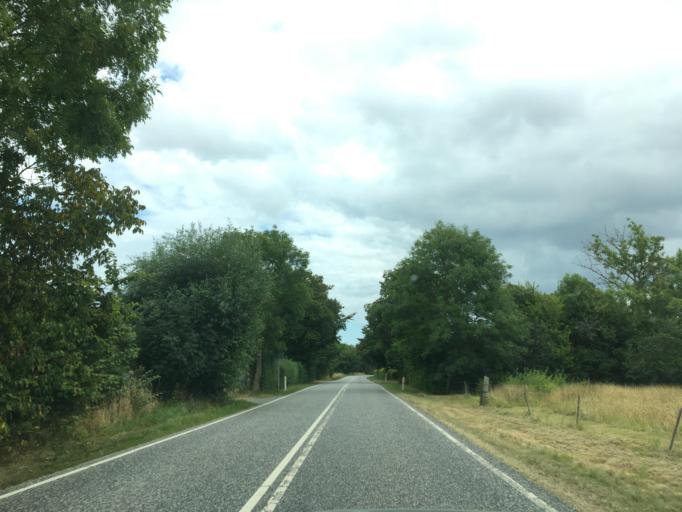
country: DK
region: South Denmark
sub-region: Nyborg Kommune
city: Ullerslev
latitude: 55.3199
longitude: 10.6946
